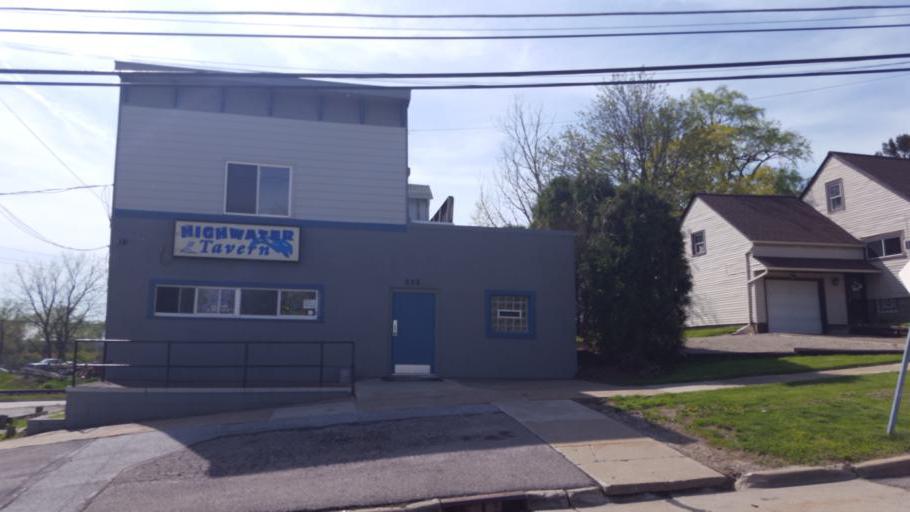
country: US
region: Ohio
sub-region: Lake County
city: Fairport Harbor
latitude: 41.7458
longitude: -81.2769
